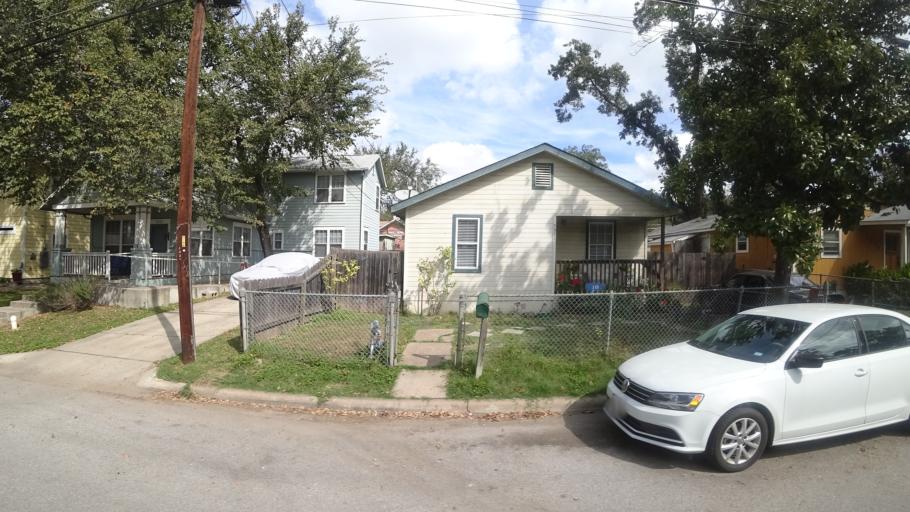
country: US
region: Texas
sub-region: Travis County
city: Austin
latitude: 30.2570
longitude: -97.7173
